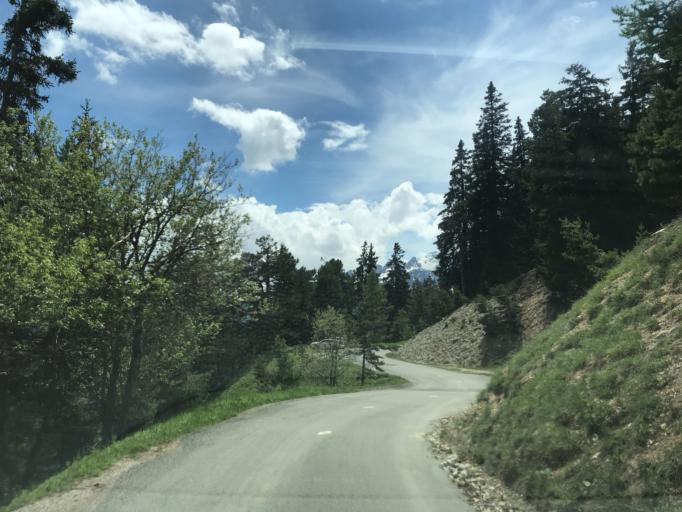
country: FR
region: Rhone-Alpes
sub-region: Departement de la Savoie
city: Modane
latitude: 45.2286
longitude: 6.6724
